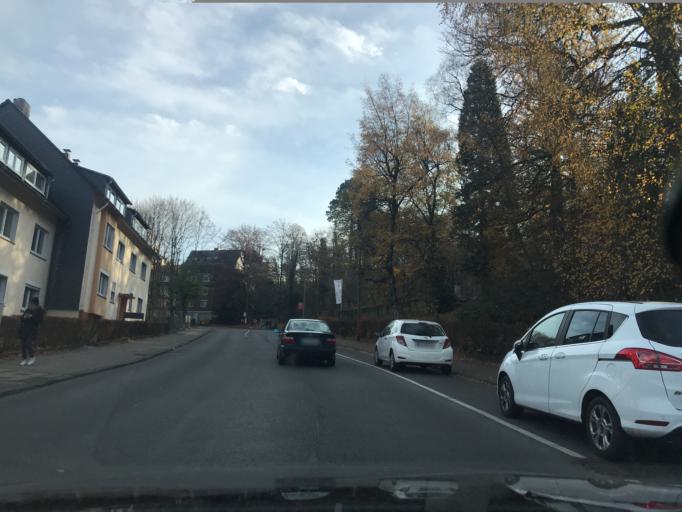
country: DE
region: North Rhine-Westphalia
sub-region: Regierungsbezirk Dusseldorf
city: Remscheid
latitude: 51.1894
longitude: 7.1724
